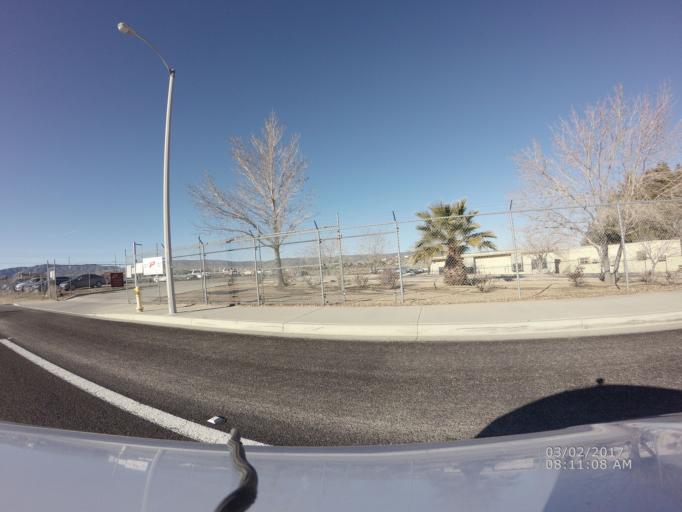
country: US
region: California
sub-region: Los Angeles County
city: Quartz Hill
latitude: 34.6474
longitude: -118.1832
